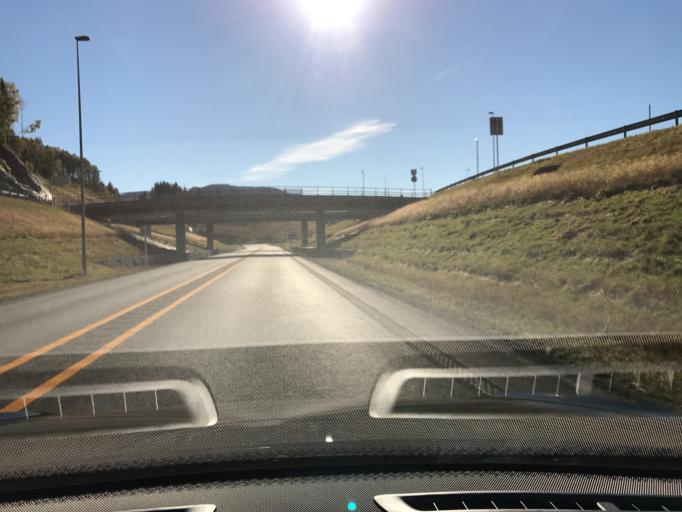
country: NO
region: Buskerud
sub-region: Krodsherad
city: Noresund
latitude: 60.2951
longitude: 9.6819
